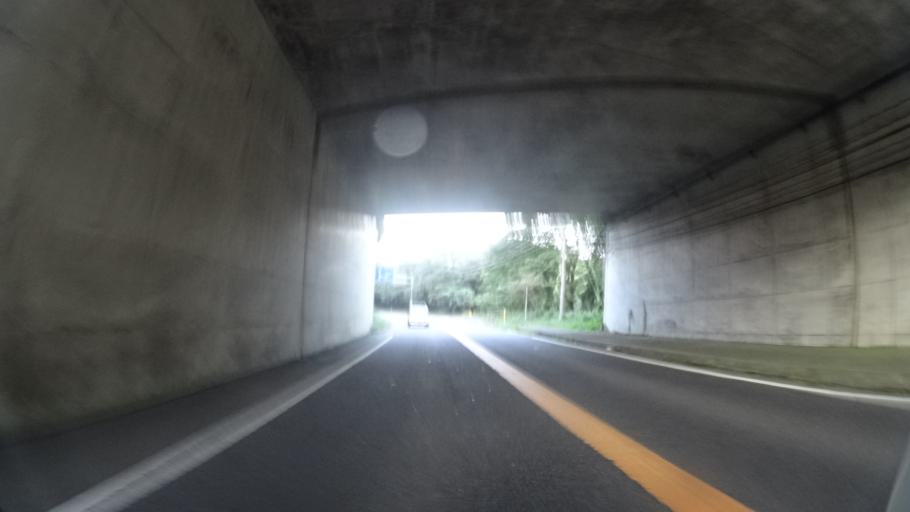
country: JP
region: Oita
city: Beppu
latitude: 33.3434
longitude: 131.4267
